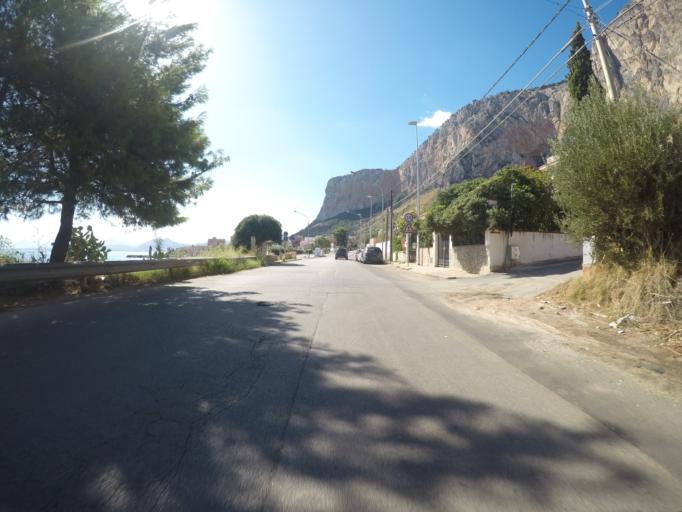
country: IT
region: Sicily
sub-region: Palermo
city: Palermo
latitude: 38.1700
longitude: 13.3667
